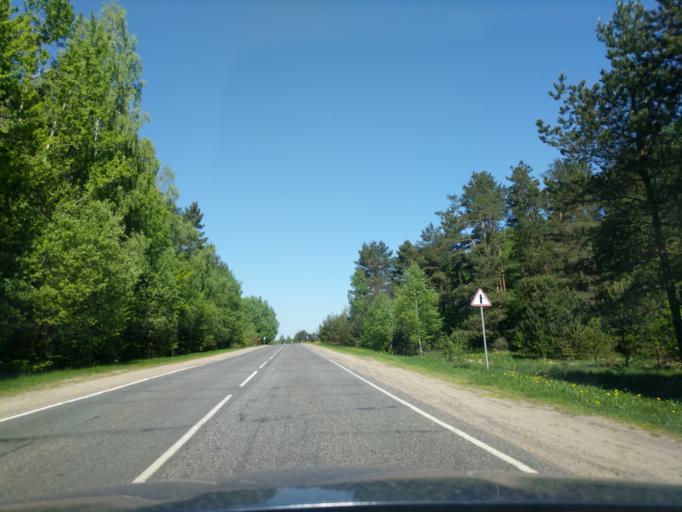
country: BY
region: Minsk
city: Myadzyel
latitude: 54.8993
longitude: 26.9044
